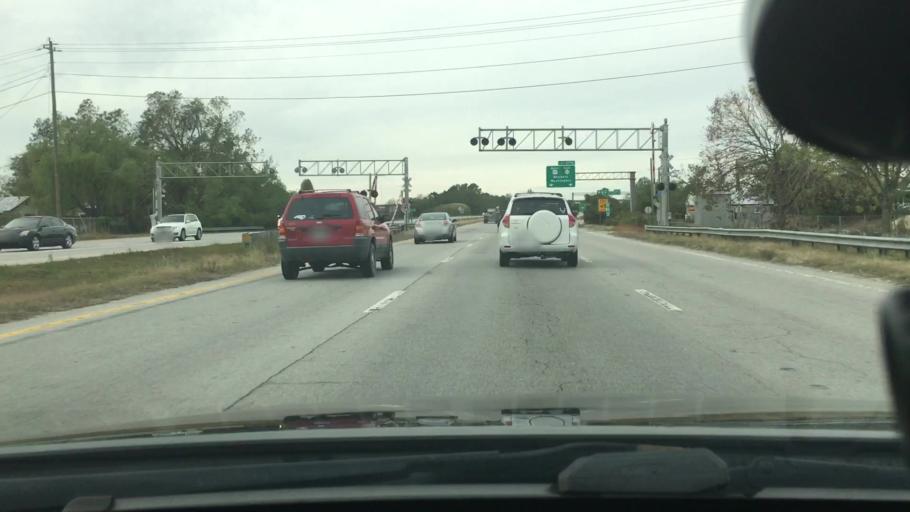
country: US
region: North Carolina
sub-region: Craven County
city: James City
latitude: 35.0882
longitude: -77.0344
